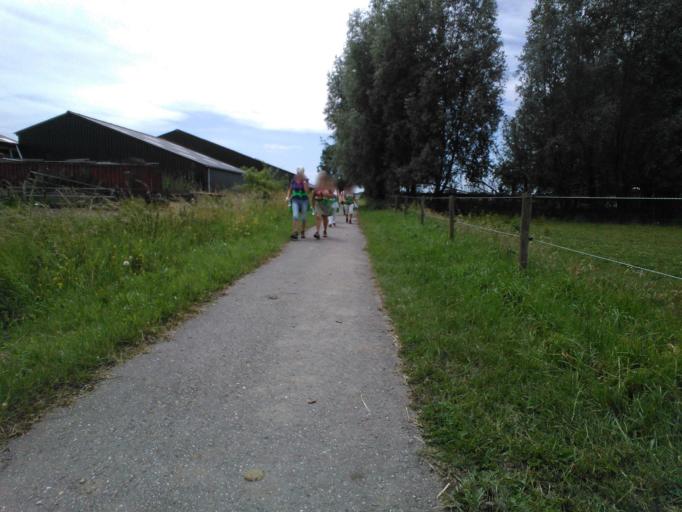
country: NL
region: South Holland
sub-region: Molenwaard
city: Nieuw-Lekkerland
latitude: 51.8742
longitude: 4.7077
